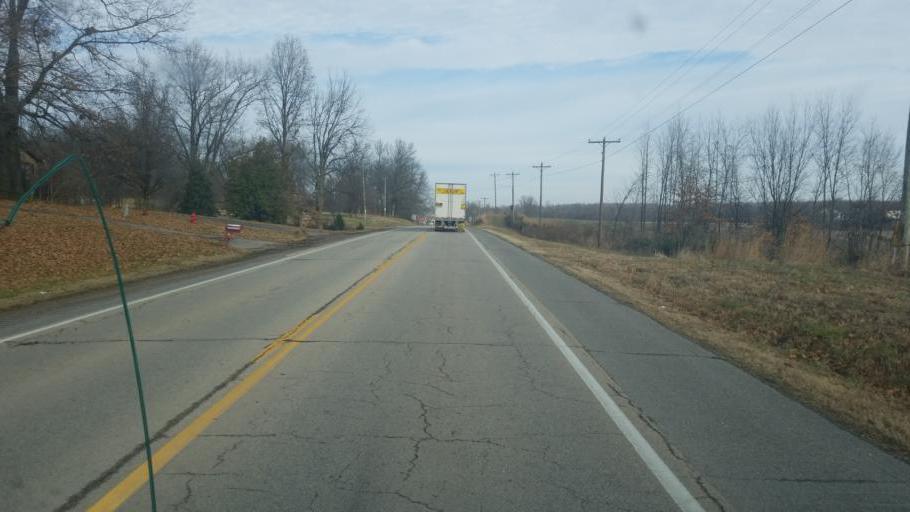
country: US
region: Missouri
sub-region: Stoddard County
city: Bloomfield
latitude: 36.8878
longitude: -89.9236
